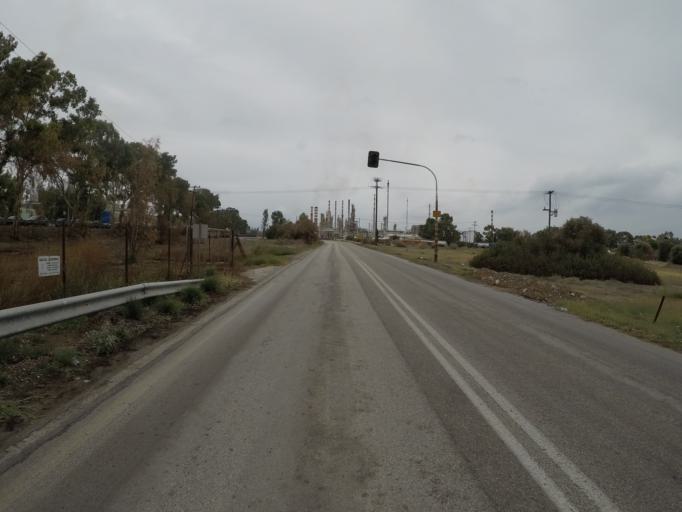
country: GR
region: Peloponnese
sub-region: Nomos Korinthias
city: Isthmia
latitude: 37.9193
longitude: 23.0635
